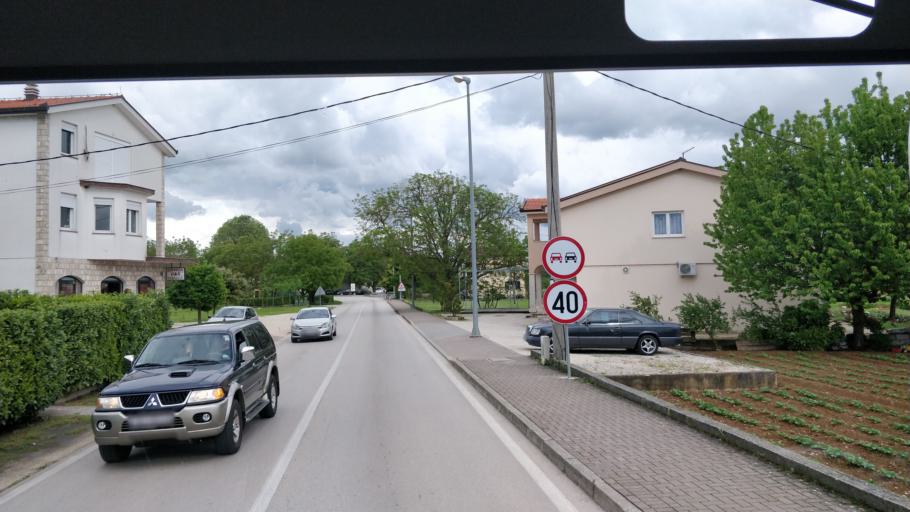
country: BA
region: Federation of Bosnia and Herzegovina
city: Ljubuski
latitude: 43.1811
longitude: 17.5183
